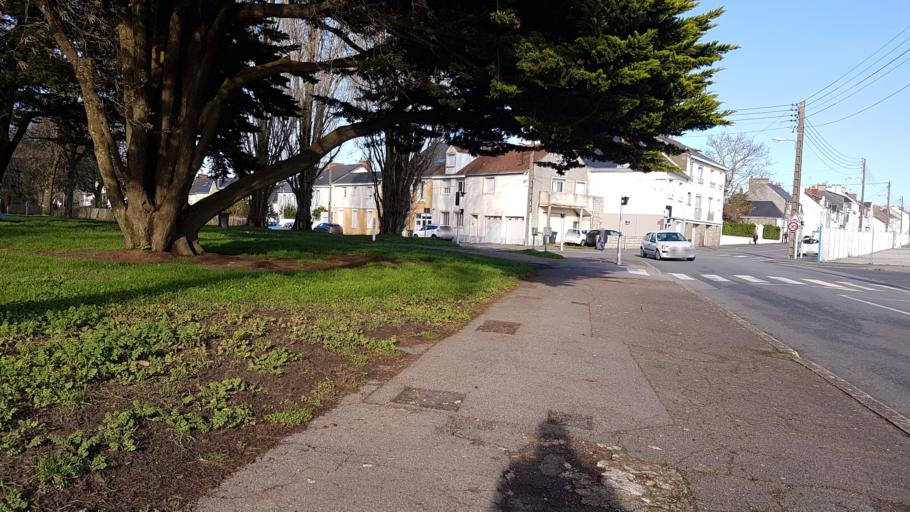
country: FR
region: Pays de la Loire
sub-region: Departement de la Loire-Atlantique
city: Saint-Nazaire
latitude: 47.2684
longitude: -2.2216
